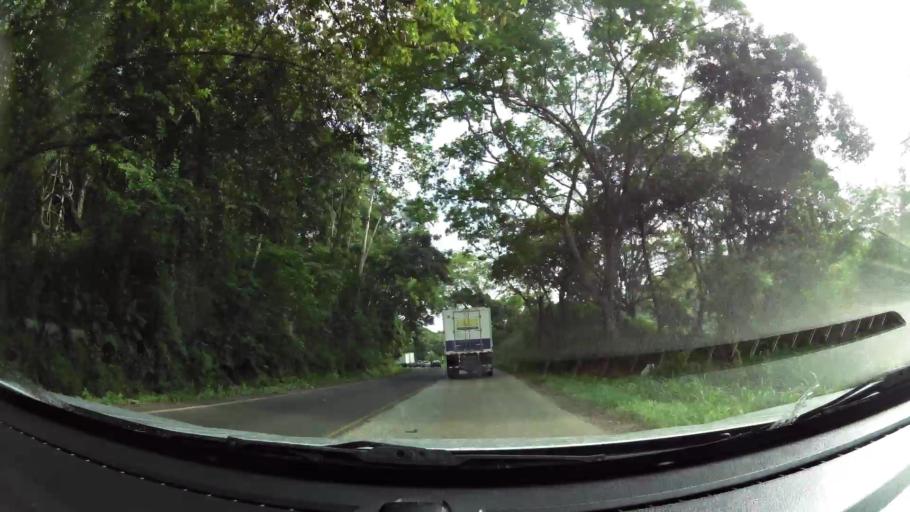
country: CR
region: Guanacaste
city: Juntas
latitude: 10.2508
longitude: -85.0561
